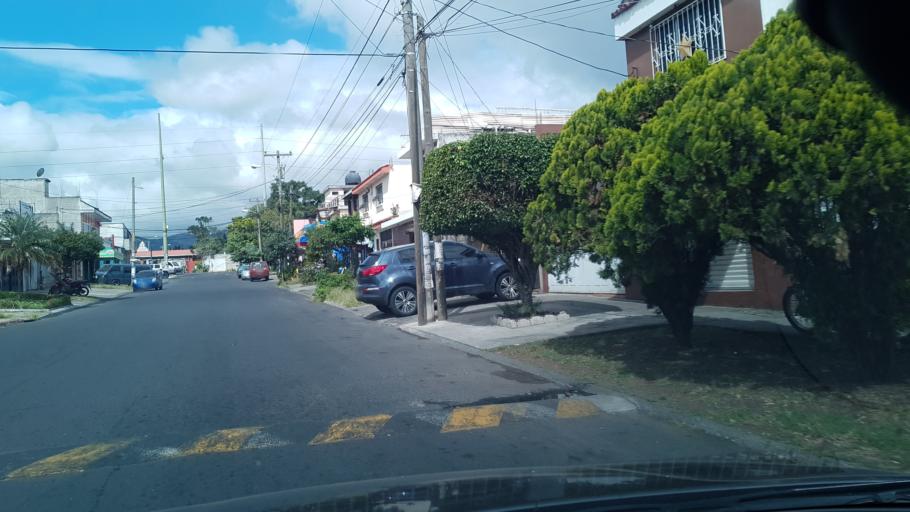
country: GT
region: Guatemala
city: Mixco
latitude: 14.6424
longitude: -90.5784
